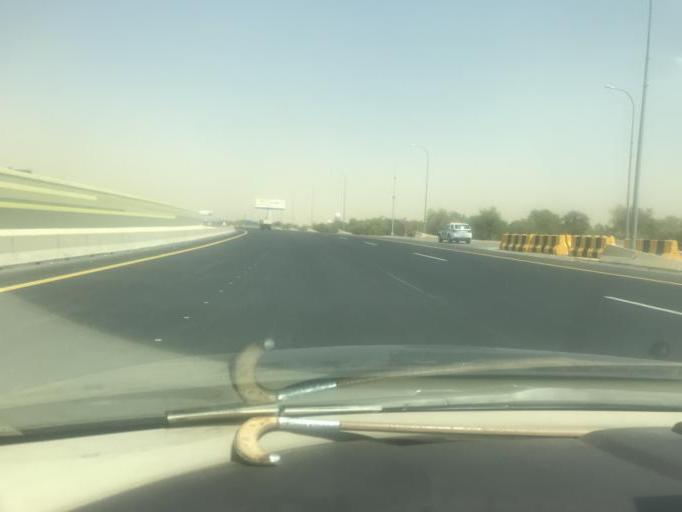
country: SA
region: Ar Riyad
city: Riyadh
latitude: 24.9183
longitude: 46.7236
